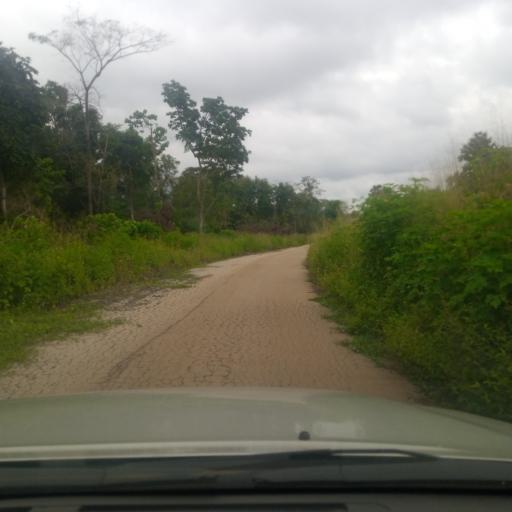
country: NG
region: Ebonyi
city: Effium
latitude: 6.6269
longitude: 8.0504
